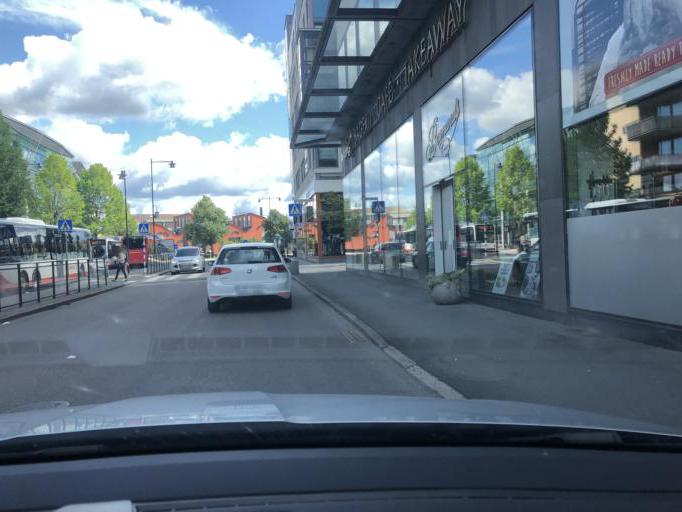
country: SE
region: Joenkoeping
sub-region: Jonkopings Kommun
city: Jonkoping
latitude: 57.7809
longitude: 14.1725
